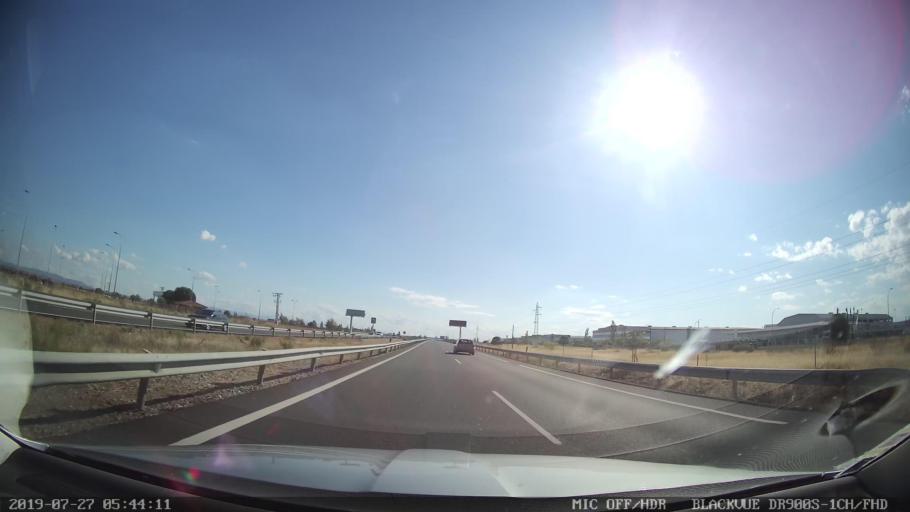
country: ES
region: Castille-La Mancha
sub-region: Province of Toledo
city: Velada
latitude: 39.9569
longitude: -4.9273
